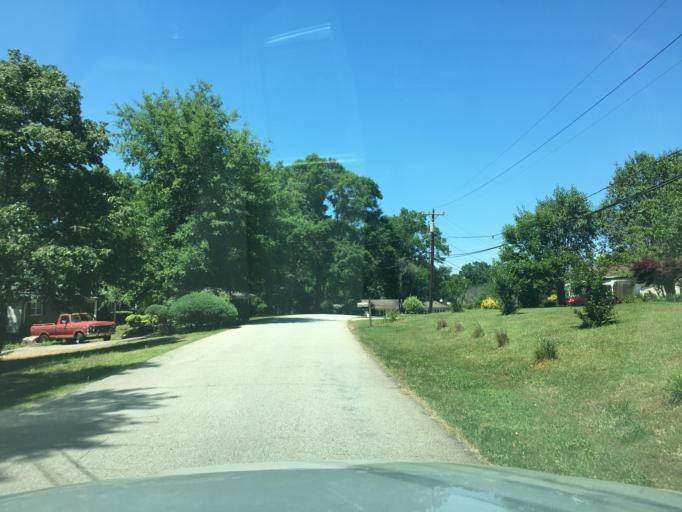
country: US
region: South Carolina
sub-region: Spartanburg County
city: Wellford
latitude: 34.9292
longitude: -82.1125
